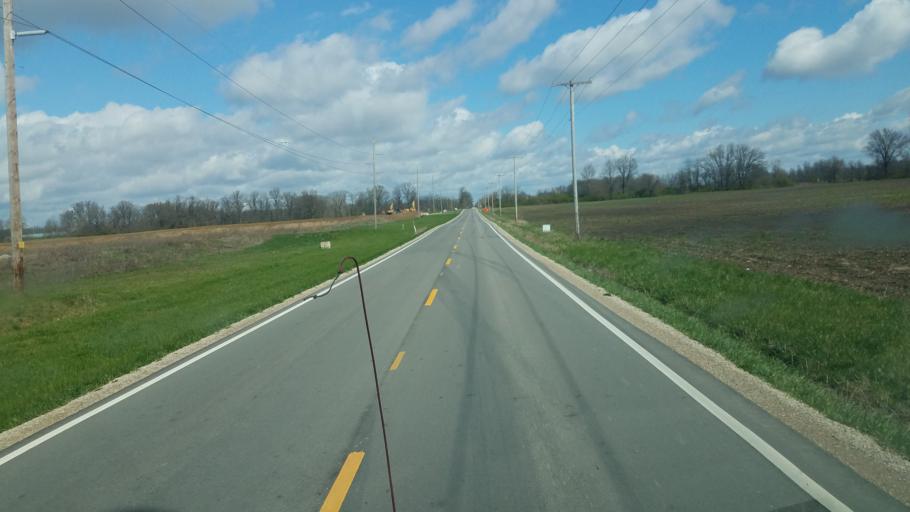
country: US
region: Ohio
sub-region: Delaware County
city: Delaware
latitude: 40.2897
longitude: -83.1276
